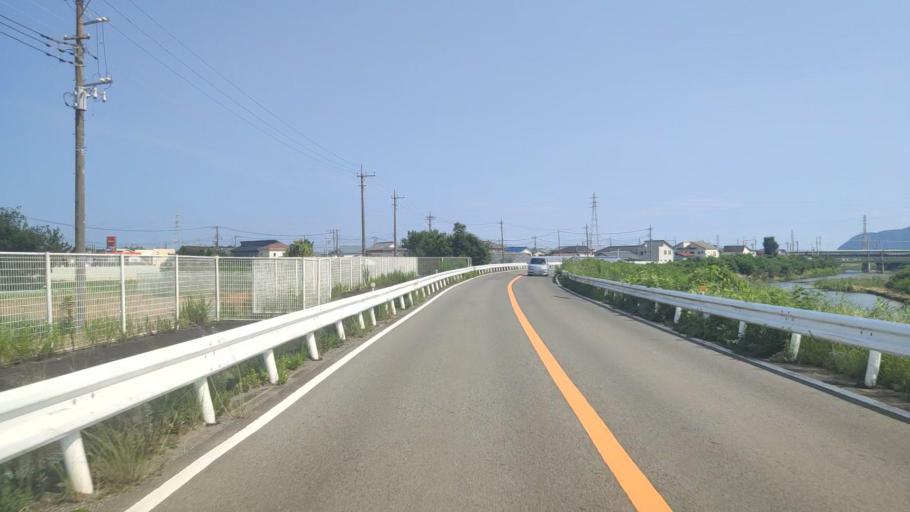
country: JP
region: Kanagawa
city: Isehara
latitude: 35.3621
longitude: 139.3233
